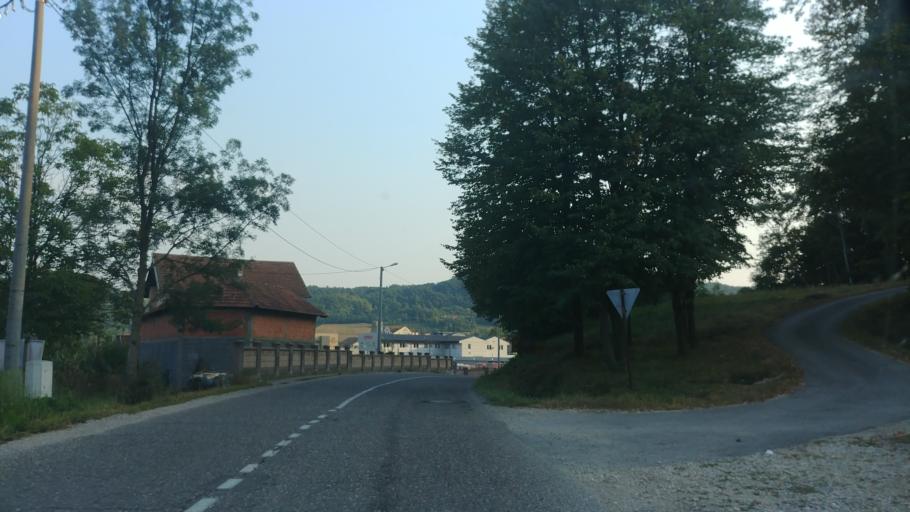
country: BA
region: Republika Srpska
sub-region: Opstina Ugljevik
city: Ugljevik
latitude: 44.6982
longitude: 18.9928
